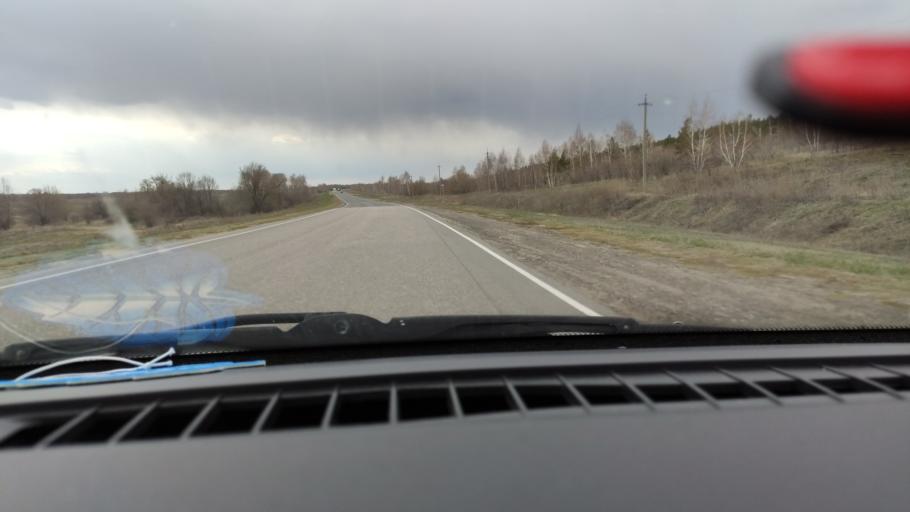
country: RU
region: Saratov
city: Sinodskoye
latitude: 52.0612
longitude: 46.7638
